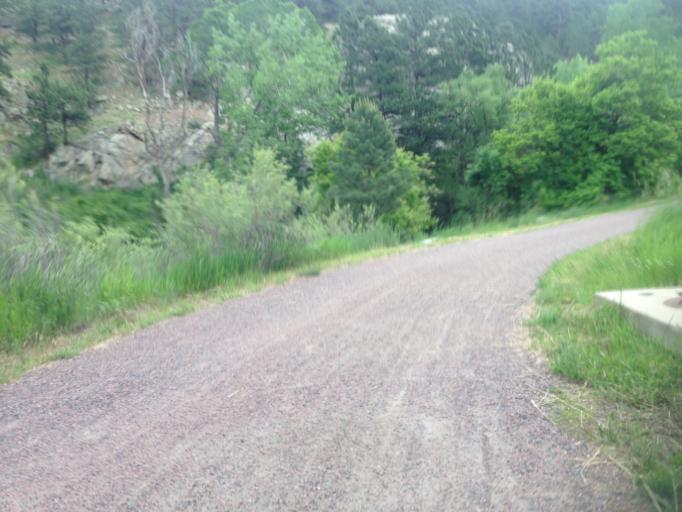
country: US
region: Colorado
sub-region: Boulder County
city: Boulder
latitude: 40.0150
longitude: -105.3208
